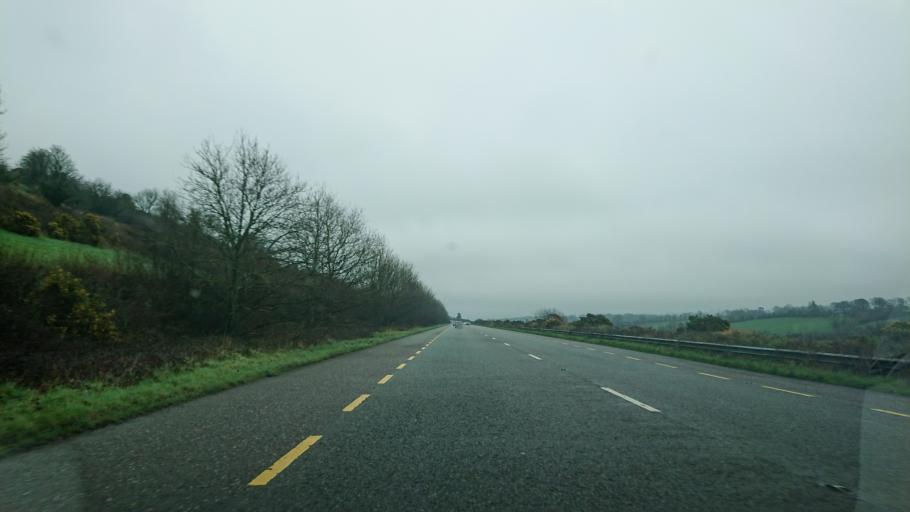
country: IE
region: Munster
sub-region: County Cork
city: Kinsale
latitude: 51.8082
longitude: -8.5545
